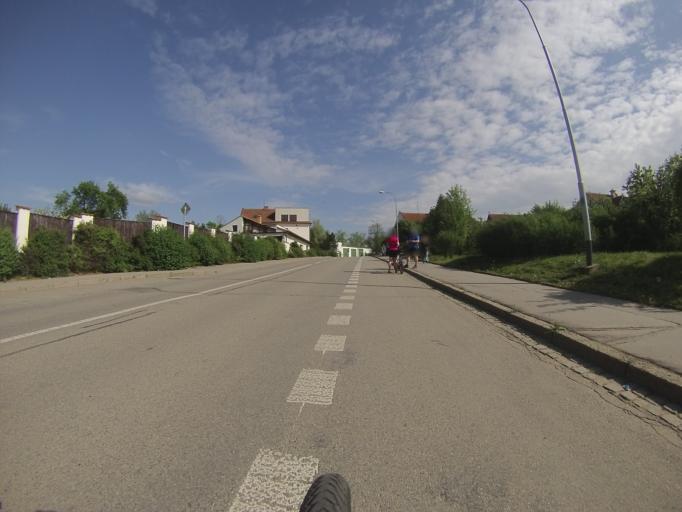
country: CZ
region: South Moravian
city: Troubsko
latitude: 49.2248
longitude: 16.5182
